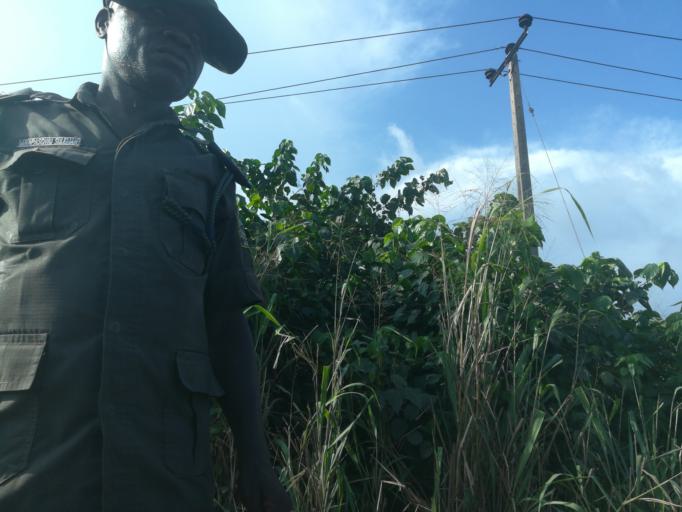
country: NG
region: Ogun
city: Ado Odo
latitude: 6.4863
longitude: 3.0627
